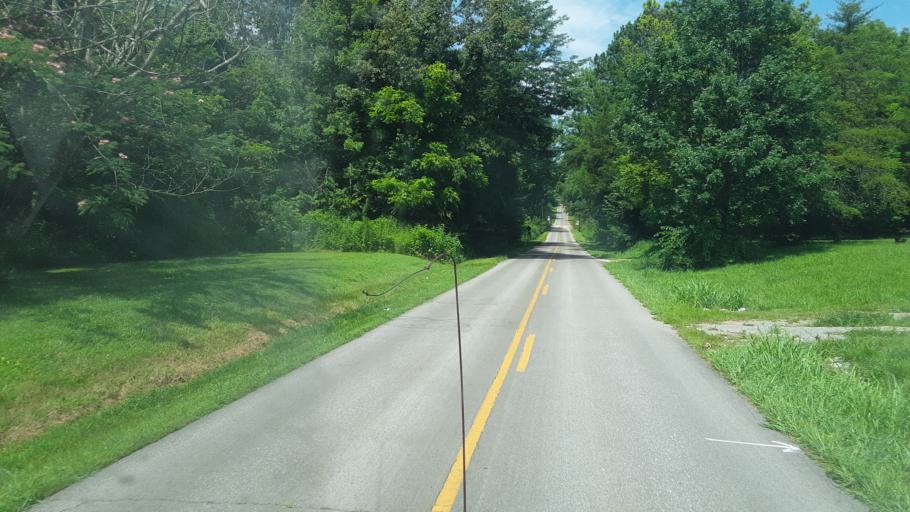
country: US
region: Kentucky
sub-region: Christian County
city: Oak Grove
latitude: 36.7311
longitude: -87.3247
